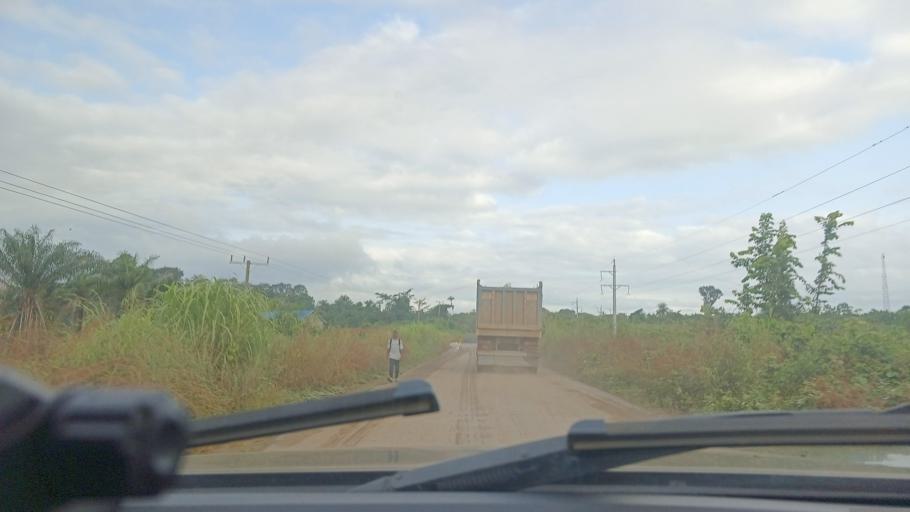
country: LR
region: Montserrado
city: Monrovia
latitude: 6.5785
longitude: -10.8876
